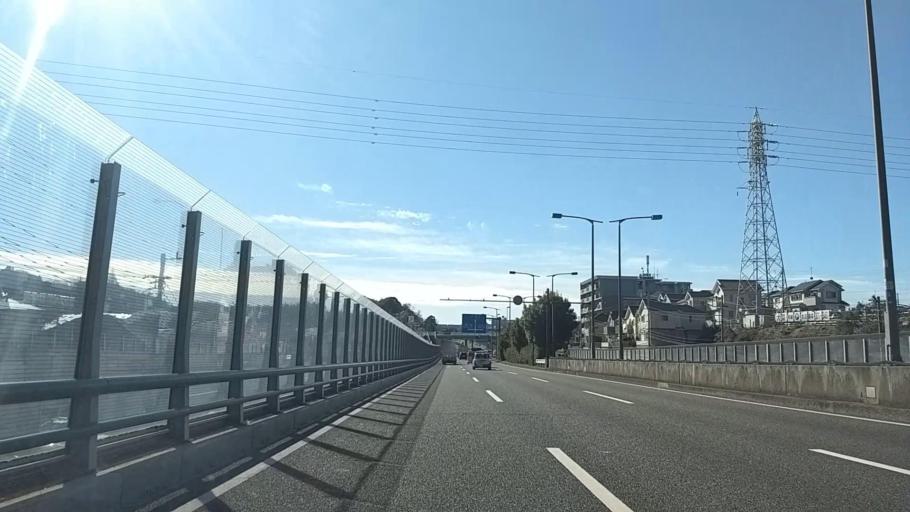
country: JP
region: Kanagawa
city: Yokohama
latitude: 35.4655
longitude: 139.5650
